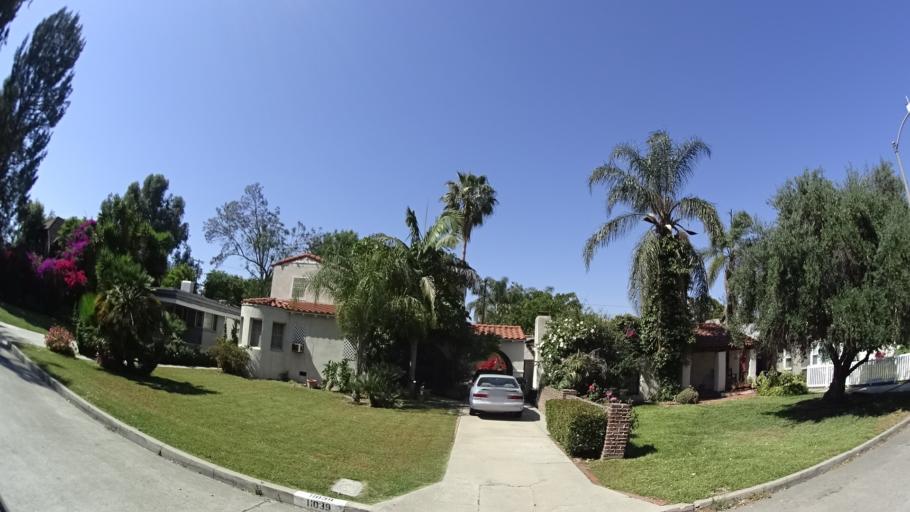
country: US
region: California
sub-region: Los Angeles County
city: North Hollywood
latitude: 34.1555
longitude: -118.3721
